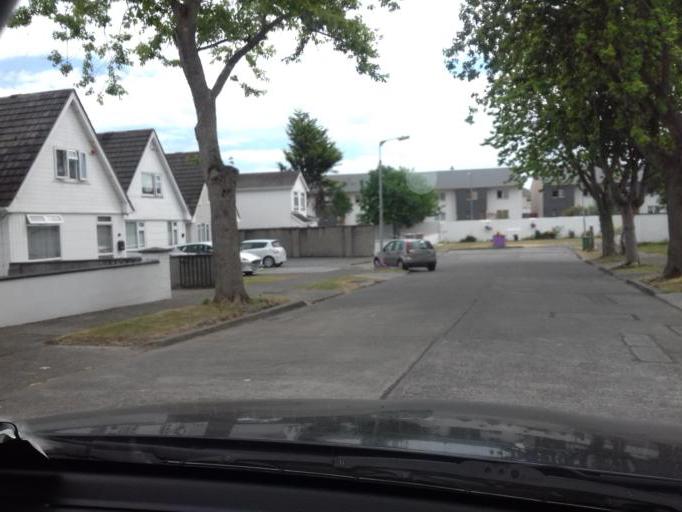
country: IE
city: Bonnybrook
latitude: 53.4022
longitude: -6.2108
